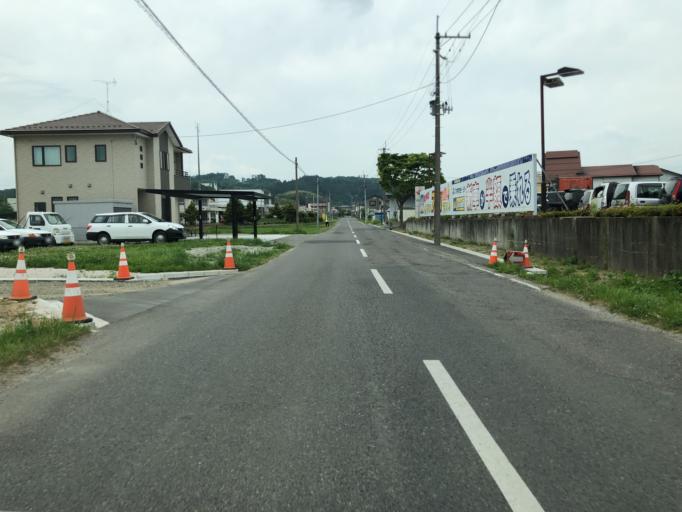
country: JP
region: Fukushima
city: Funehikimachi-funehiki
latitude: 37.4374
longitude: 140.6361
